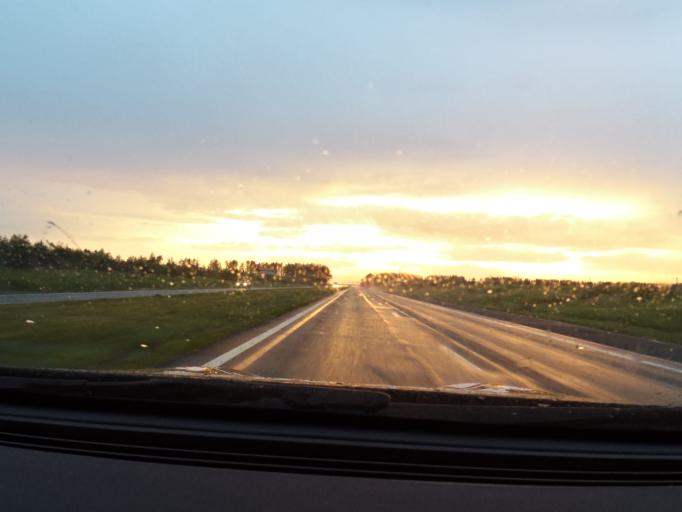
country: RU
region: Tatarstan
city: Yelabuga
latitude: 55.7963
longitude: 52.1525
